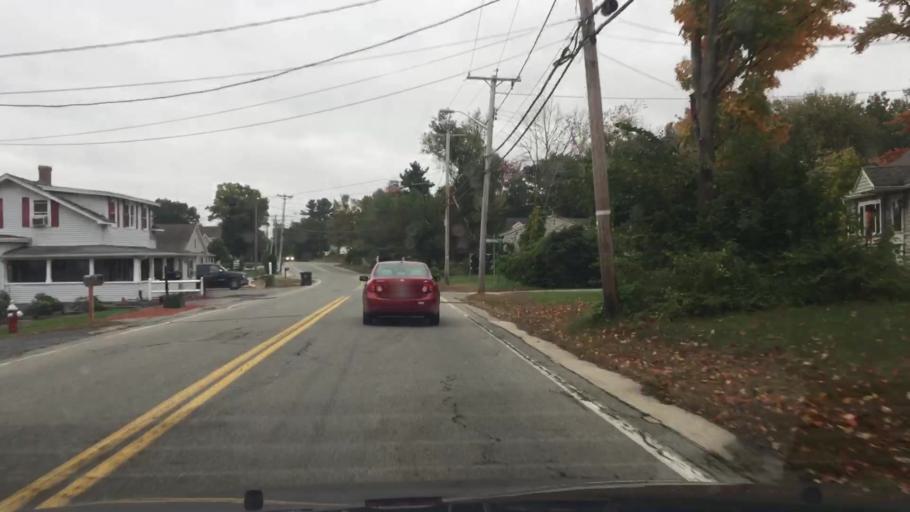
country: US
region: Massachusetts
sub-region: Middlesex County
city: Tyngsboro
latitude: 42.6827
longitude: -71.3698
